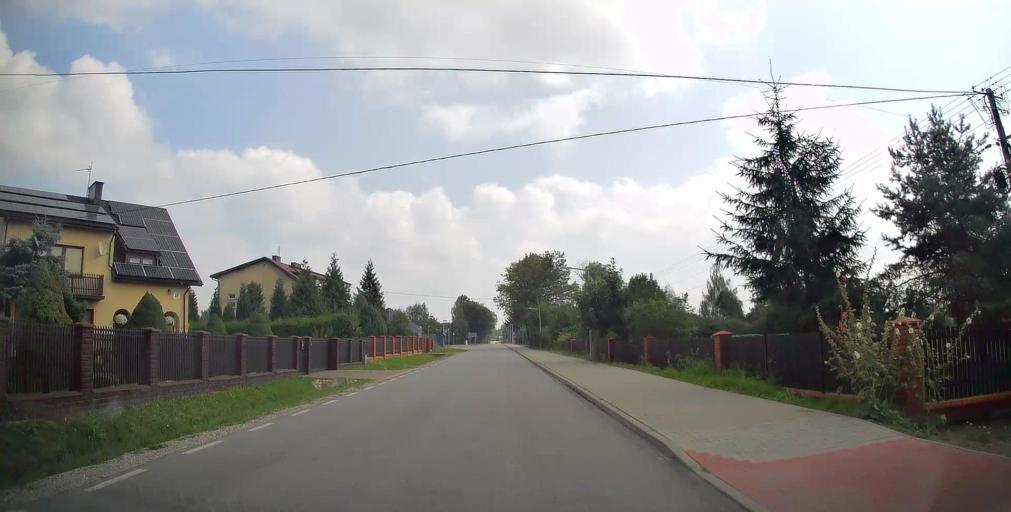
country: PL
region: Masovian Voivodeship
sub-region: Powiat bialobrzeski
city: Sucha
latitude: 51.6094
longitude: 20.9763
